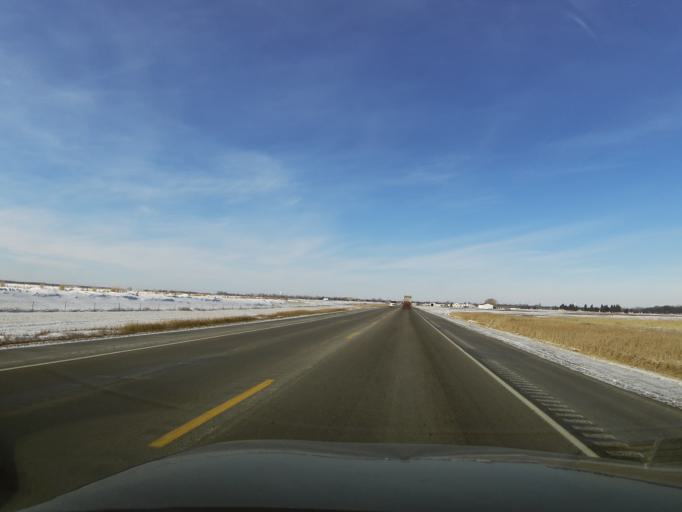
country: US
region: North Dakota
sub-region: Walsh County
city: Grafton
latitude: 48.4125
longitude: -97.3729
